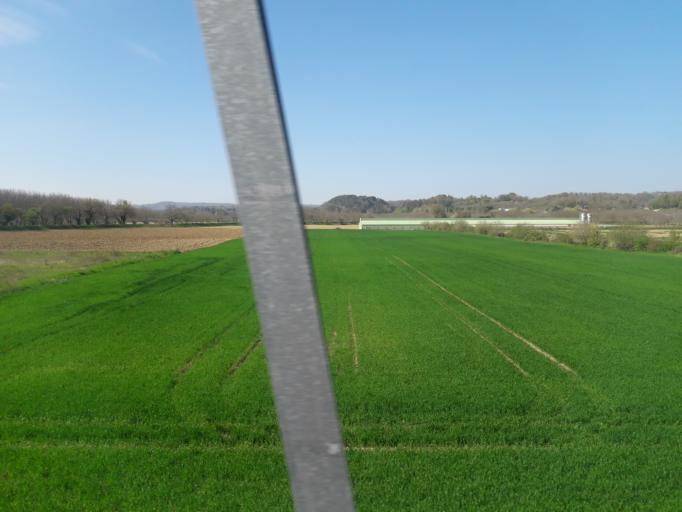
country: FR
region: Rhone-Alpes
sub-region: Departement de la Drome
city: Saint-Paul-les-Romans
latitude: 45.0733
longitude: 5.1430
